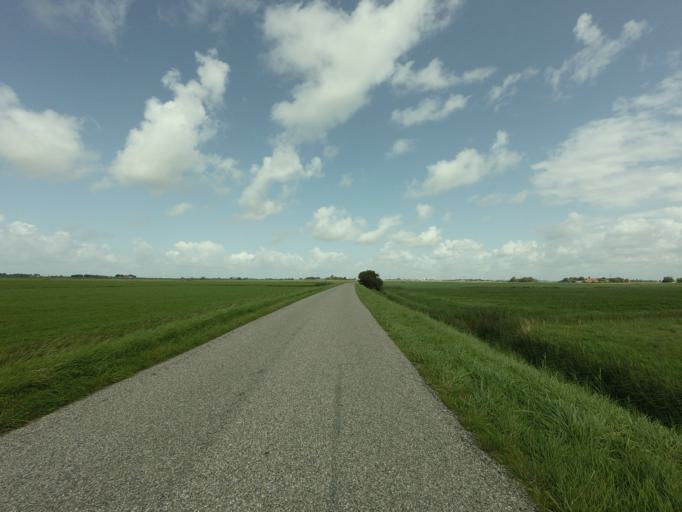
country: NL
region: Friesland
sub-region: Gemeente Franekeradeel
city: Sexbierum
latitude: 53.1613
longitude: 5.4839
